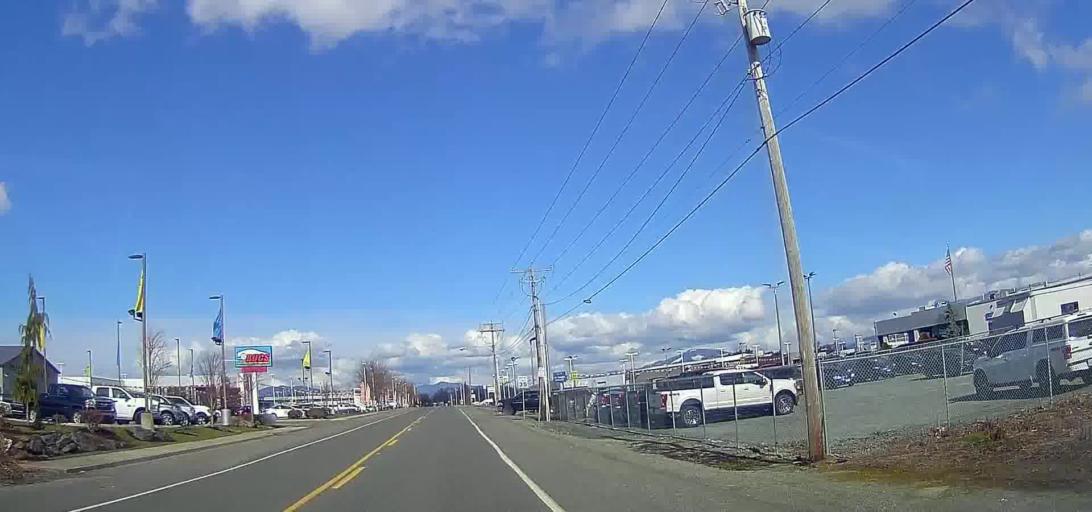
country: US
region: Washington
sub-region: Skagit County
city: Mount Vernon
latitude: 48.4478
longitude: -122.3450
